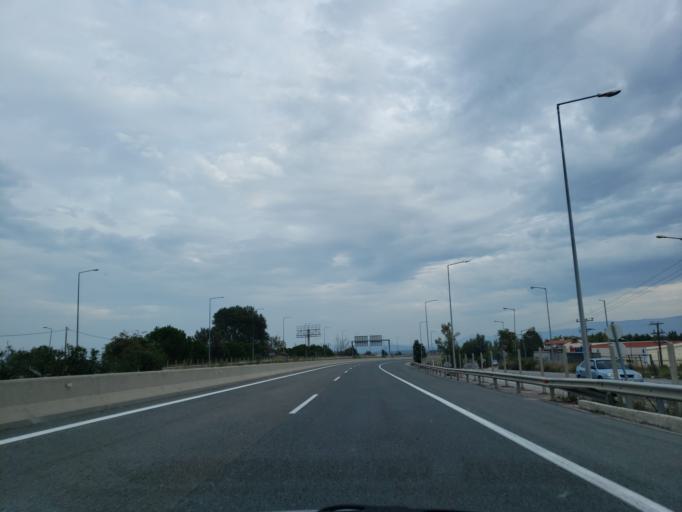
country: GR
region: Central Greece
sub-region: Nomos Voiotias
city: Schimatari
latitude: 38.3503
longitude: 23.5836
